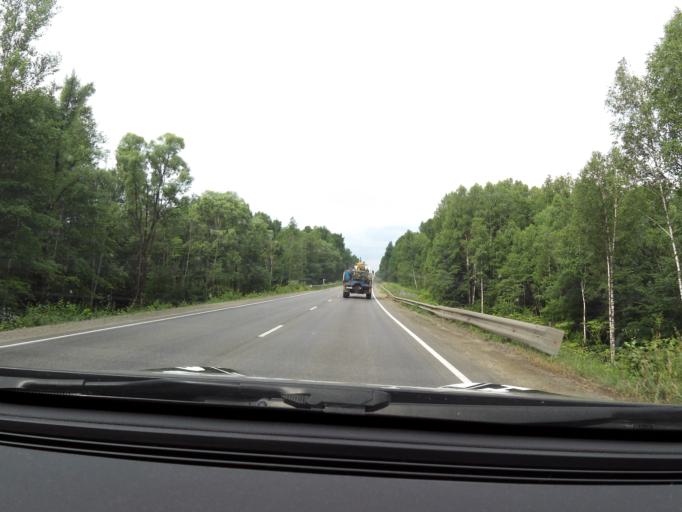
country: RU
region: Chelyabinsk
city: Asha
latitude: 54.8857
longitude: 57.2889
